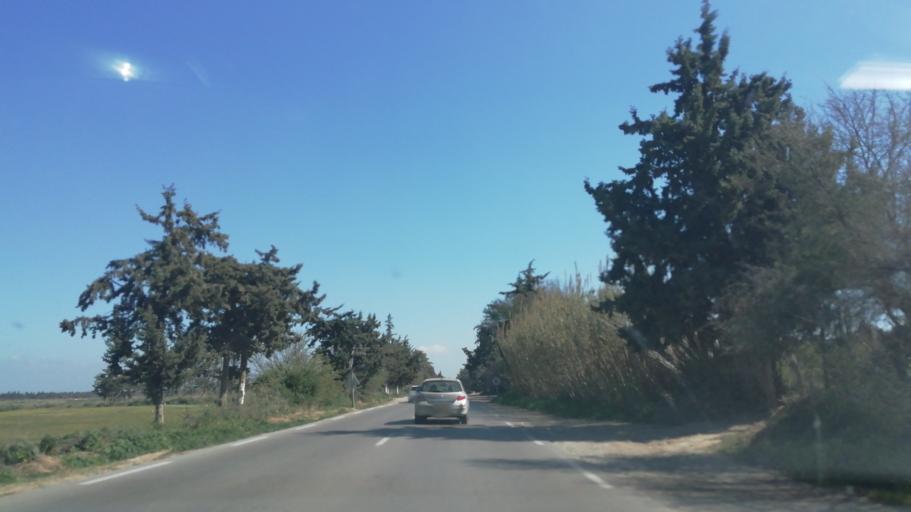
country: DZ
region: Mascara
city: Sig
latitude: 35.5733
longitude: -0.0171
